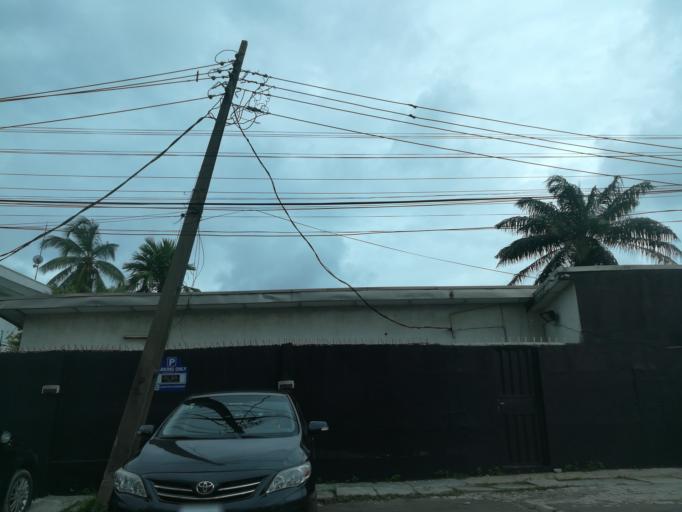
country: NG
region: Lagos
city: Ikoyi
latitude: 6.4348
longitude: 3.4151
